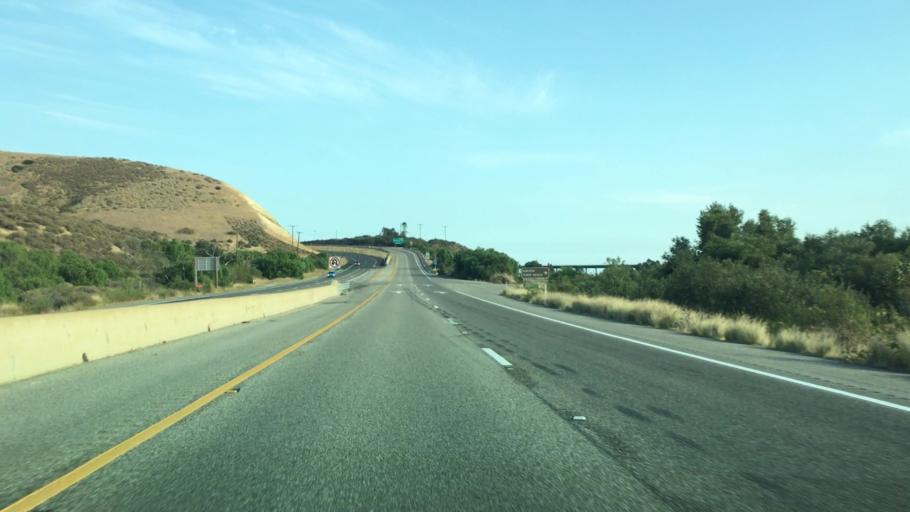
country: US
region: California
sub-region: Santa Barbara County
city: Buellton
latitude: 34.4788
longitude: -120.2290
